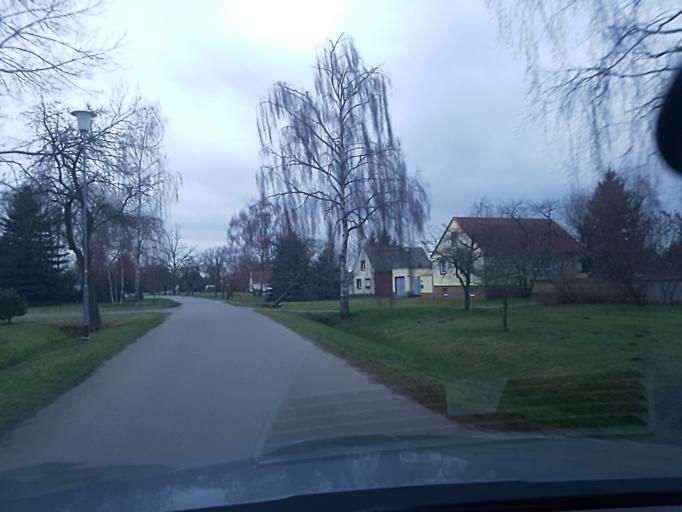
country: DE
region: Brandenburg
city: Schonewalde
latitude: 51.6804
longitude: 13.5997
